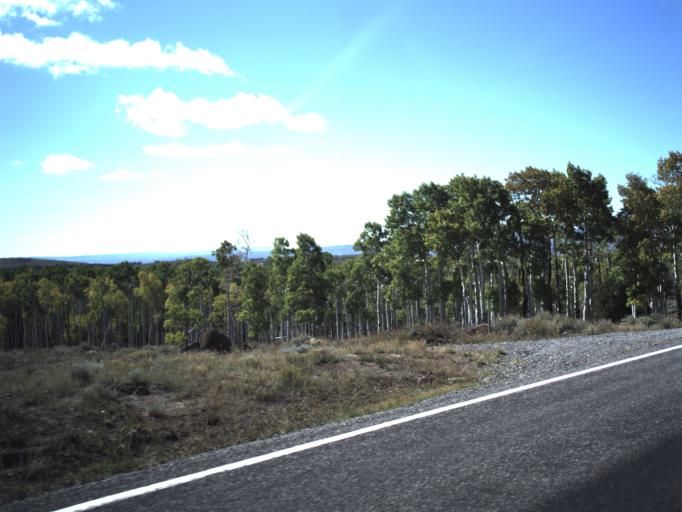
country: US
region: Utah
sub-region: Wayne County
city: Loa
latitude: 38.5142
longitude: -111.7661
